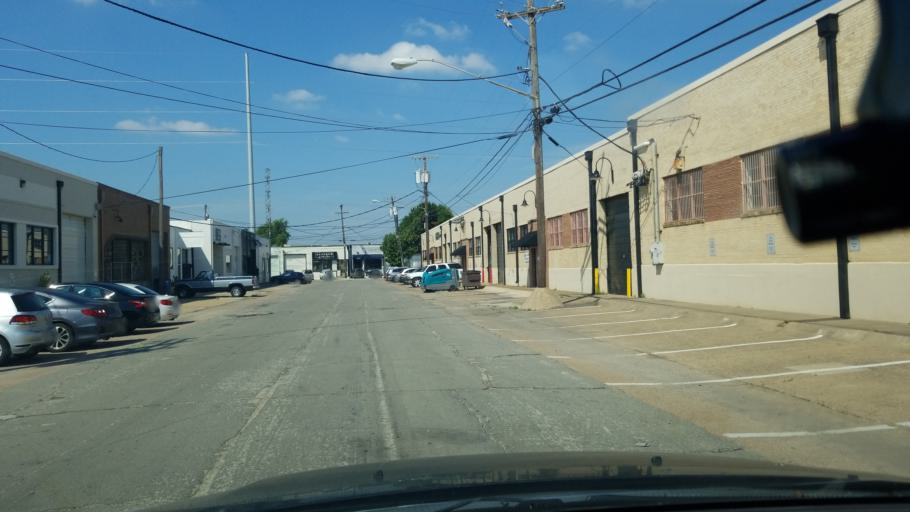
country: US
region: Texas
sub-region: Dallas County
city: Dallas
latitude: 32.7888
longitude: -96.8223
